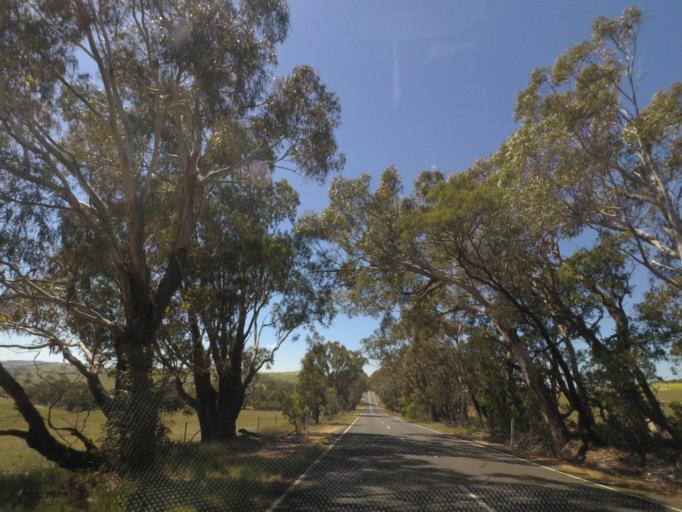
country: AU
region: Victoria
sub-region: Hume
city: Sunbury
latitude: -37.1814
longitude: 144.7443
